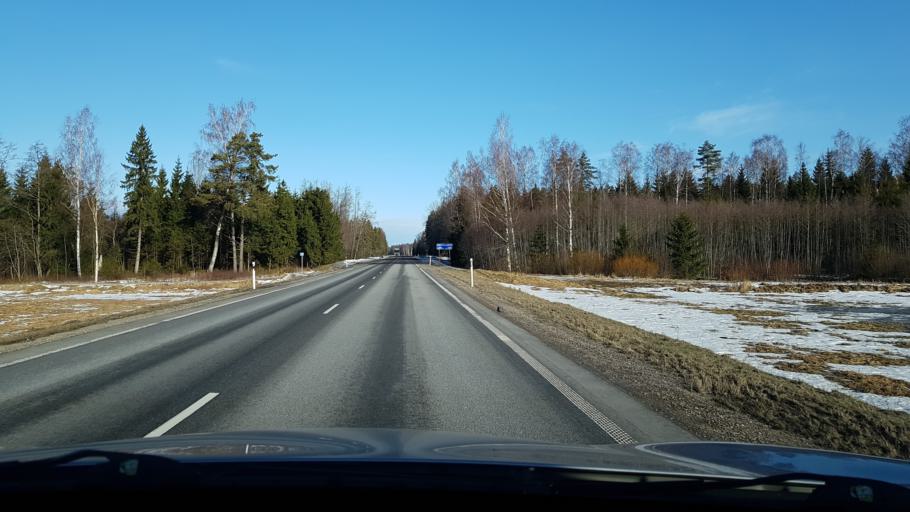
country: EE
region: Viljandimaa
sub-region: Vohma linn
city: Vohma
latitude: 58.5874
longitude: 25.5709
